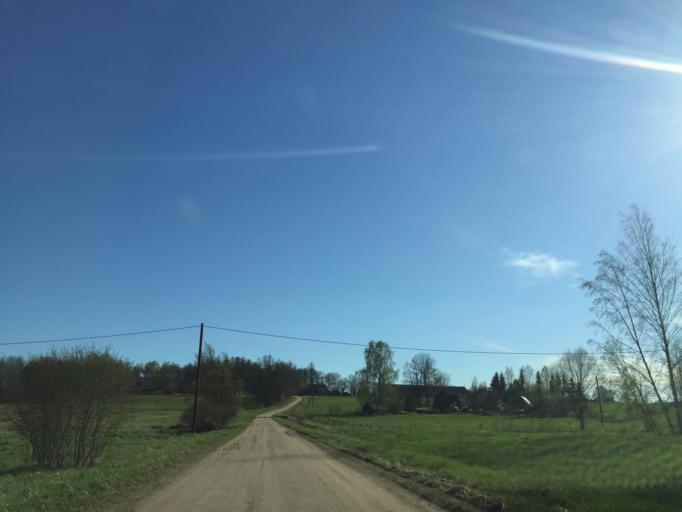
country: EE
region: Valgamaa
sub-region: Valga linn
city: Valga
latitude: 57.7680
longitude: 26.2151
